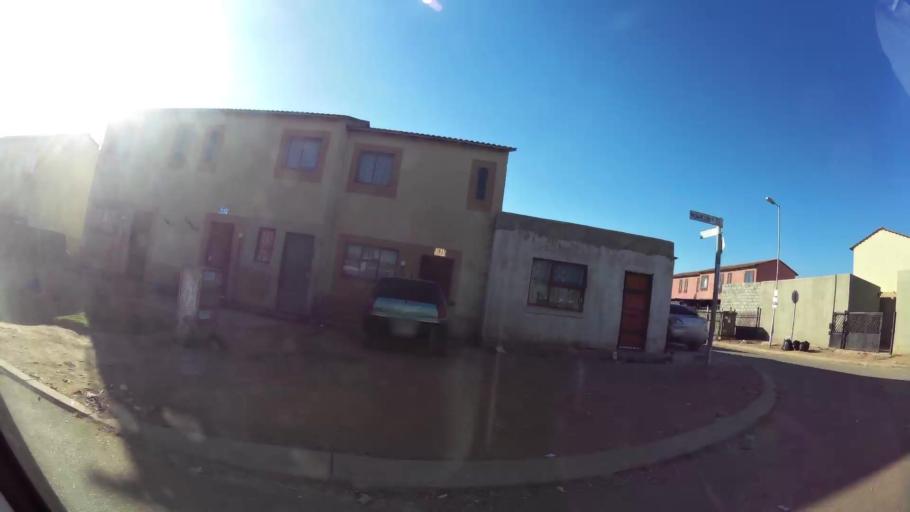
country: ZA
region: Gauteng
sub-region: City of Johannesburg Metropolitan Municipality
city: Diepsloot
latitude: -25.9026
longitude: 28.0912
